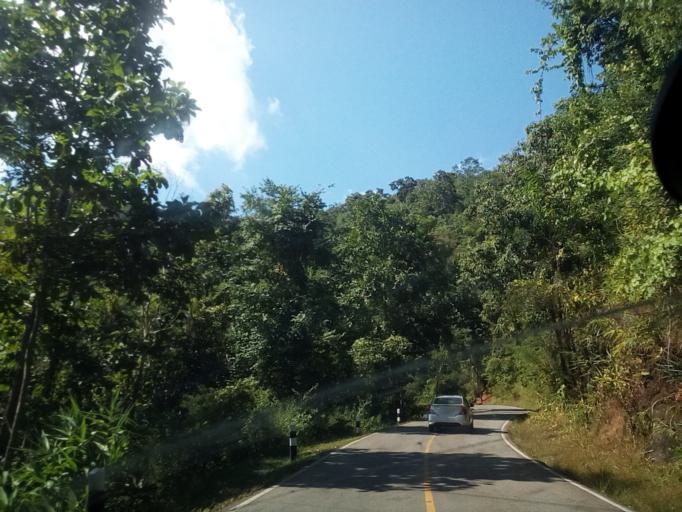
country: TH
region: Chiang Mai
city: Samoeng
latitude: 18.8560
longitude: 98.6866
